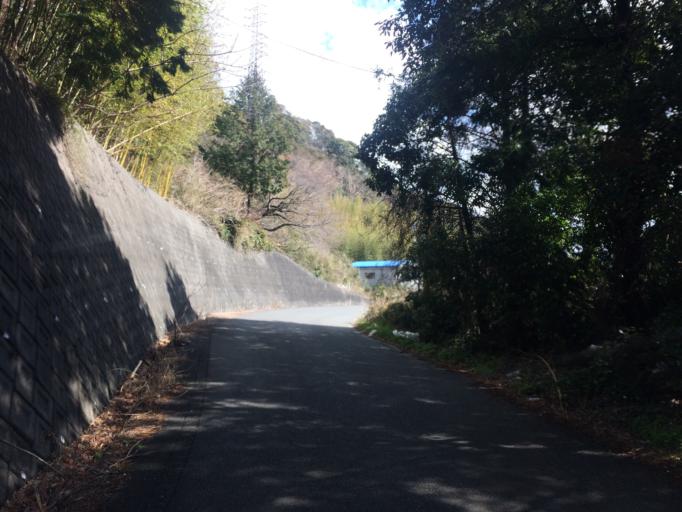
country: JP
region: Shizuoka
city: Shimada
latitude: 34.7666
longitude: 138.1967
